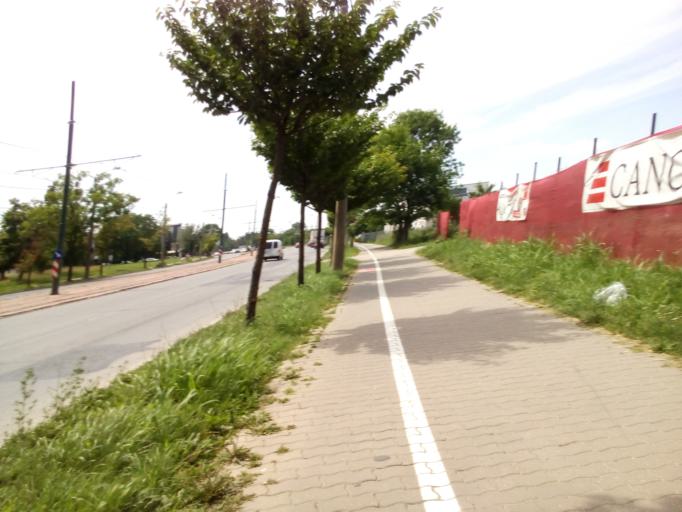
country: RO
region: Timis
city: Timisoara
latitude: 45.7365
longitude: 21.2528
